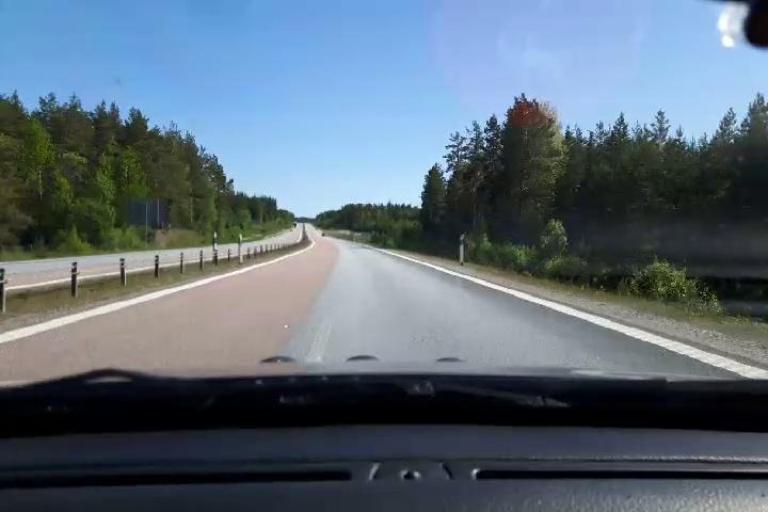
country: SE
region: Gaevleborg
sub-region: Soderhamns Kommun
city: Soderhamn
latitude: 61.3323
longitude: 17.0196
